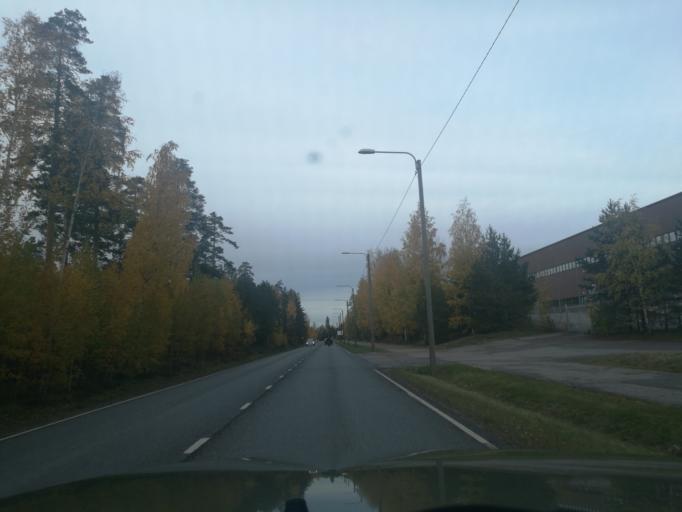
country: FI
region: Uusimaa
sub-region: Helsinki
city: Vantaa
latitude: 60.3020
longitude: 25.0901
